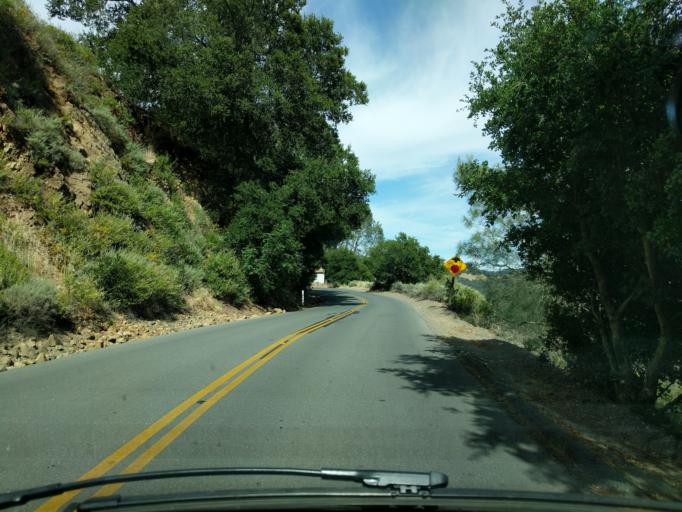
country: US
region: California
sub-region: Contra Costa County
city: Blackhawk
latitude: 37.8425
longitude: -121.9215
